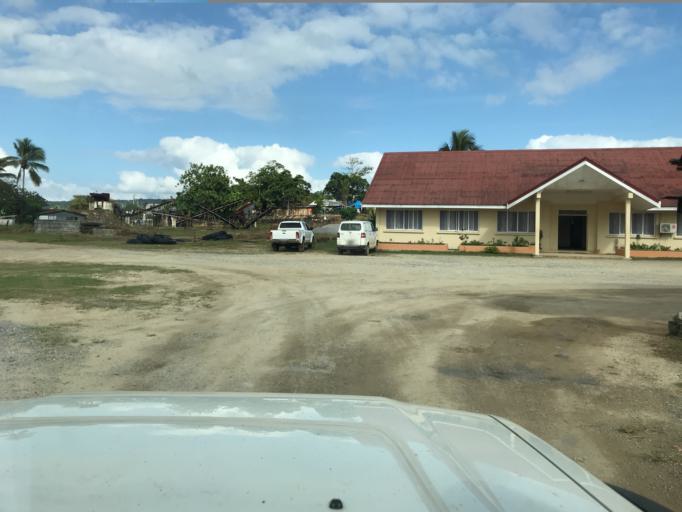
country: VU
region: Sanma
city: Luganville
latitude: -15.5148
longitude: 167.1657
